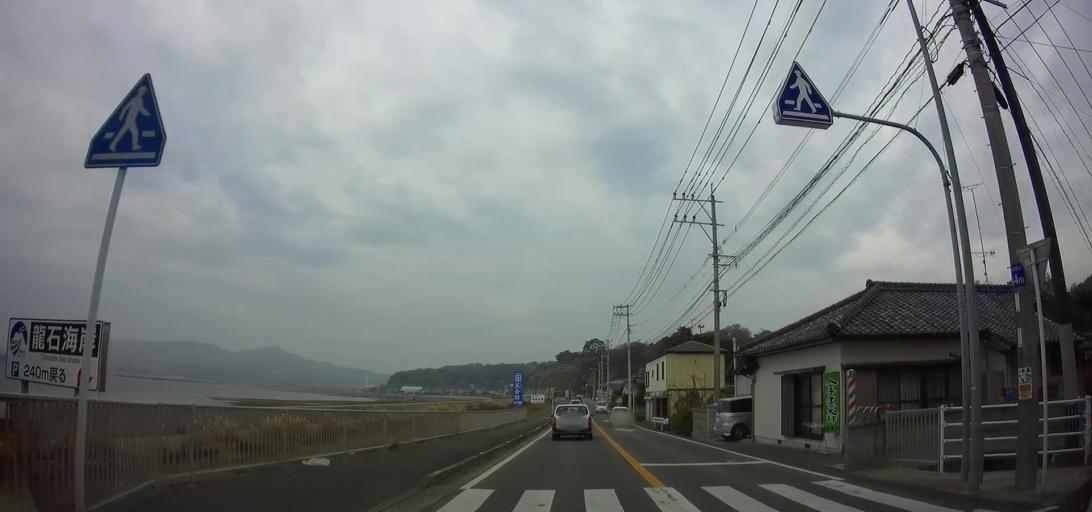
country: JP
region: Nagasaki
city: Shimabara
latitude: 32.6532
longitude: 130.2803
